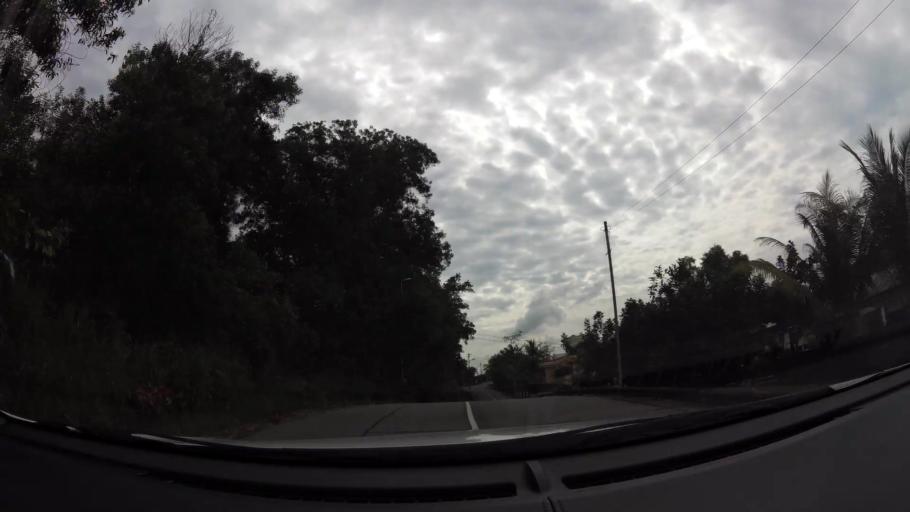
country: BN
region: Brunei and Muara
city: Bandar Seri Begawan
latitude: 4.8862
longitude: 114.9095
